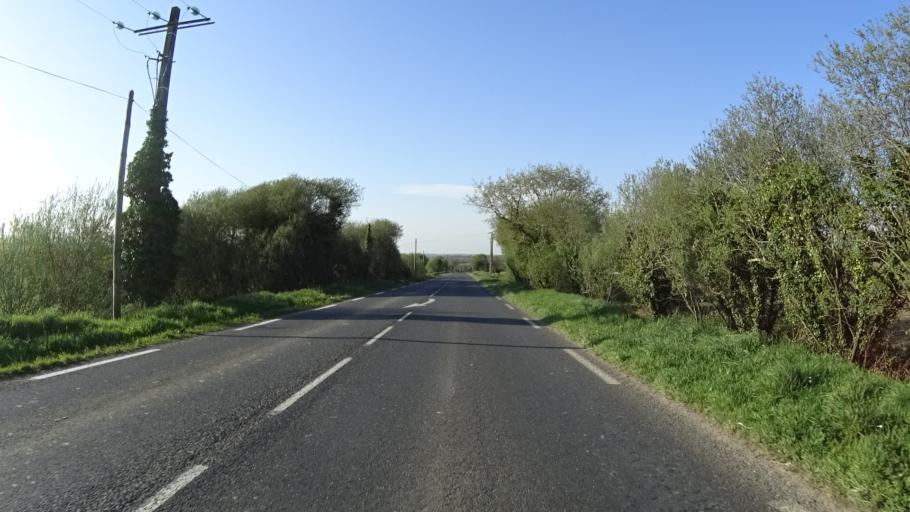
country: FR
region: Brittany
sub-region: Departement du Finistere
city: La Roche-Maurice
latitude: 48.4411
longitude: -4.1830
